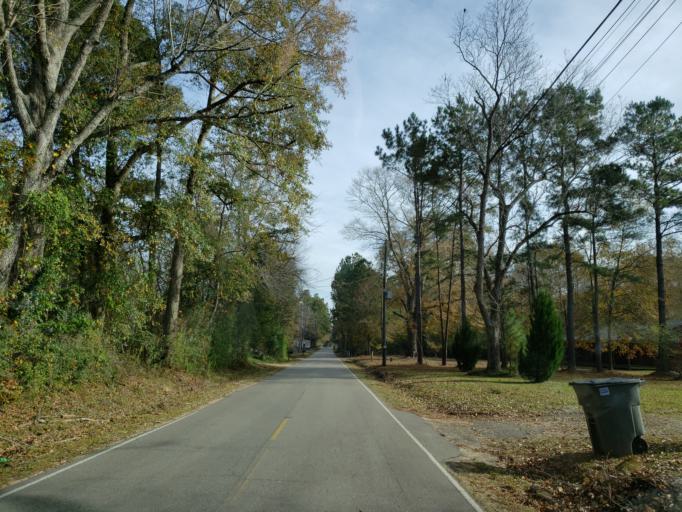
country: US
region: Mississippi
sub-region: Forrest County
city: Rawls Springs
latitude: 31.3957
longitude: -89.3877
